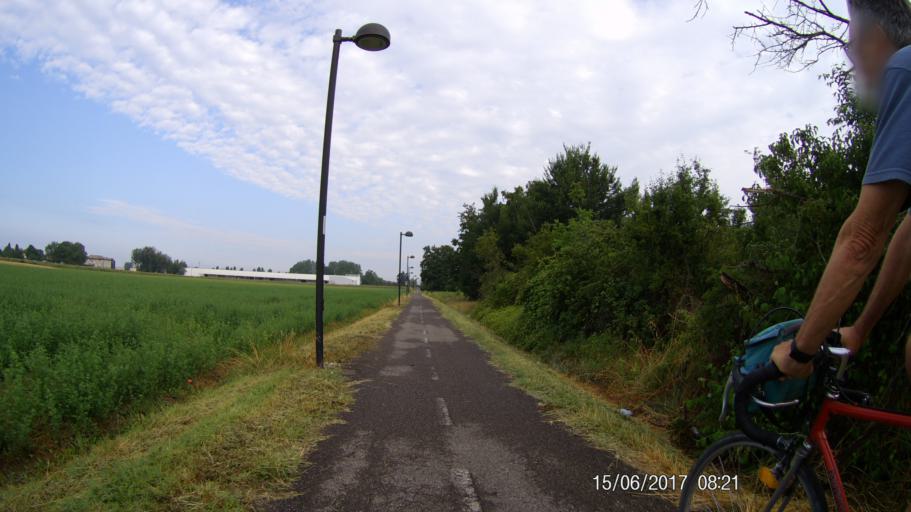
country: IT
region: Emilia-Romagna
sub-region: Provincia di Reggio Emilia
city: Roncocesi
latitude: 44.7188
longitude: 10.5723
